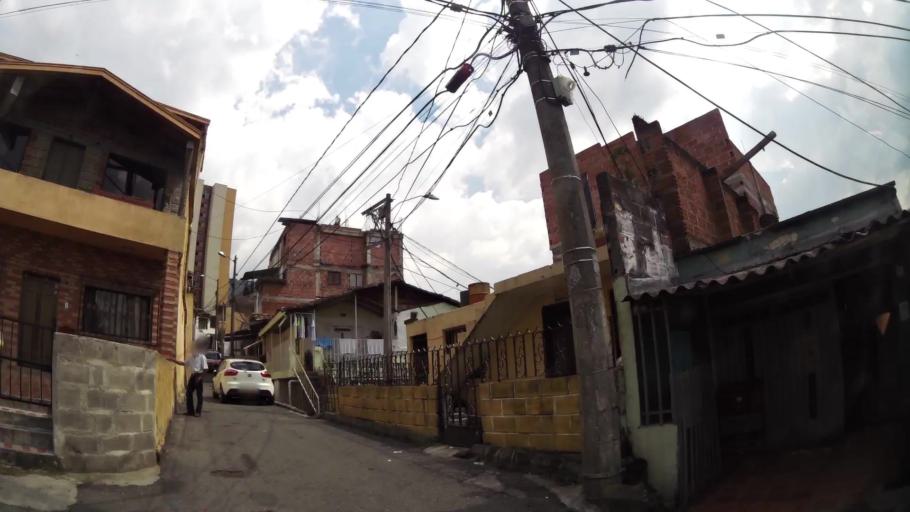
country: CO
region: Antioquia
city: Sabaneta
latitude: 6.1558
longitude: -75.6012
